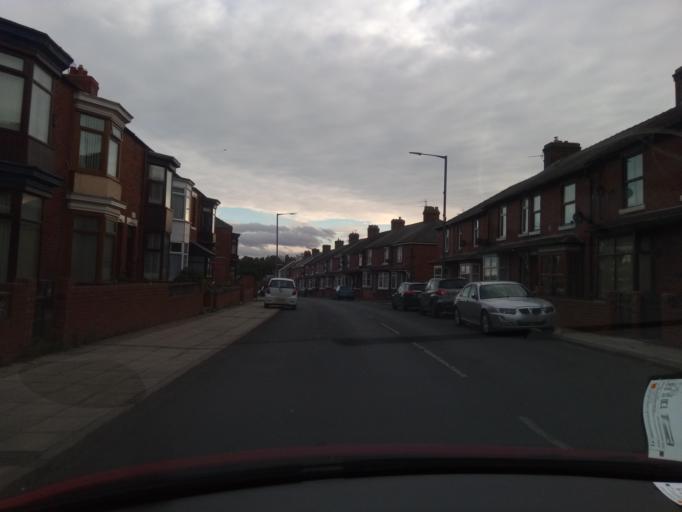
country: GB
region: England
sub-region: County Durham
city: Shildon
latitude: 54.6305
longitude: -1.6536
